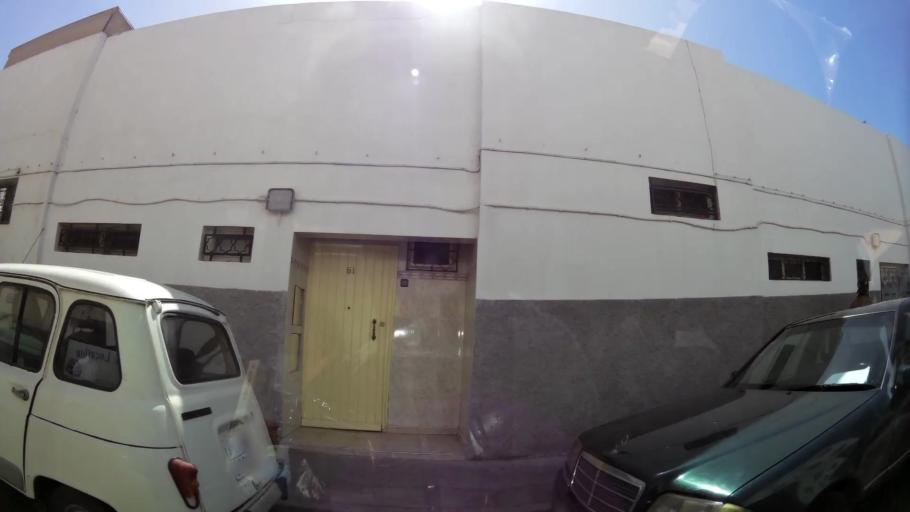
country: MA
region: Souss-Massa-Draa
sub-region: Agadir-Ida-ou-Tnan
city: Agadir
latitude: 30.4118
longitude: -9.5852
